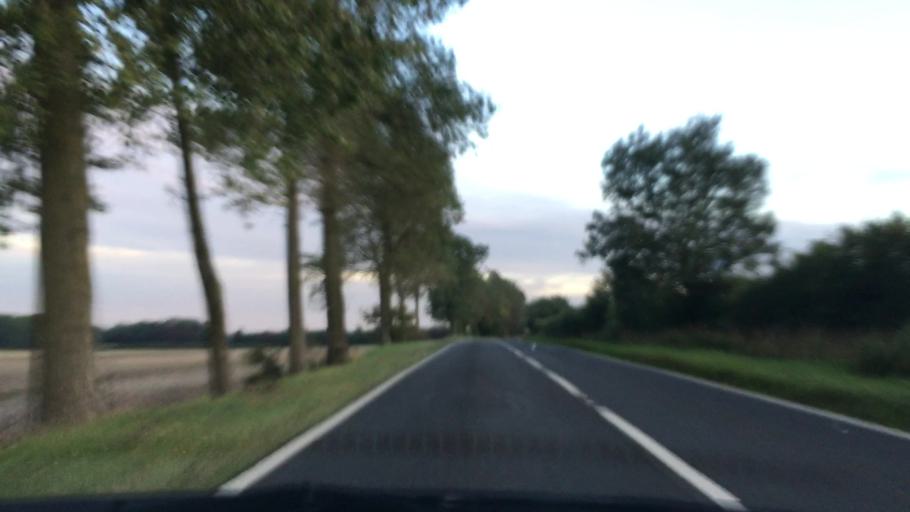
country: GB
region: England
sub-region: North East Lincolnshire
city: Wold Newton
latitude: 53.4721
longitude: -0.1106
